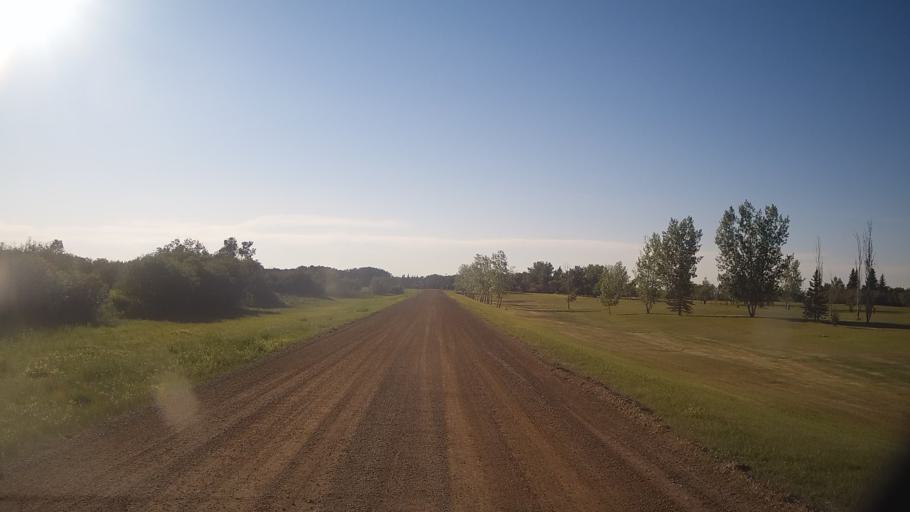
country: CA
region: Saskatchewan
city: Lanigan
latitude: 51.8486
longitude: -105.0133
